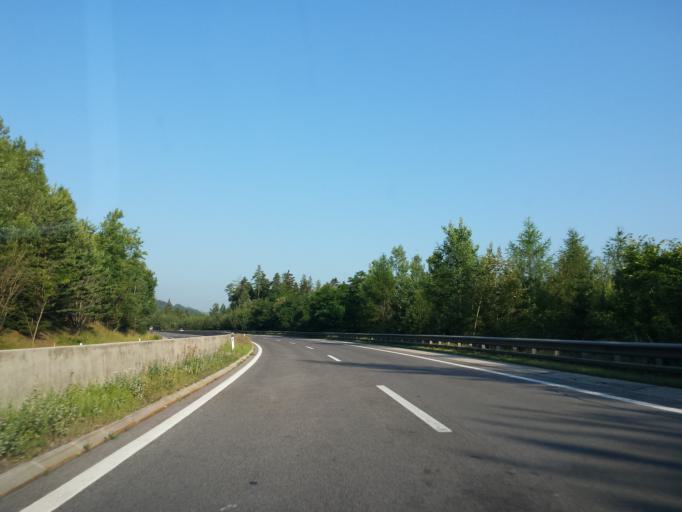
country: AT
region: Lower Austria
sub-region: Politischer Bezirk Neunkirchen
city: Raach am Hochgebirge
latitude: 47.6556
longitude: 15.9090
